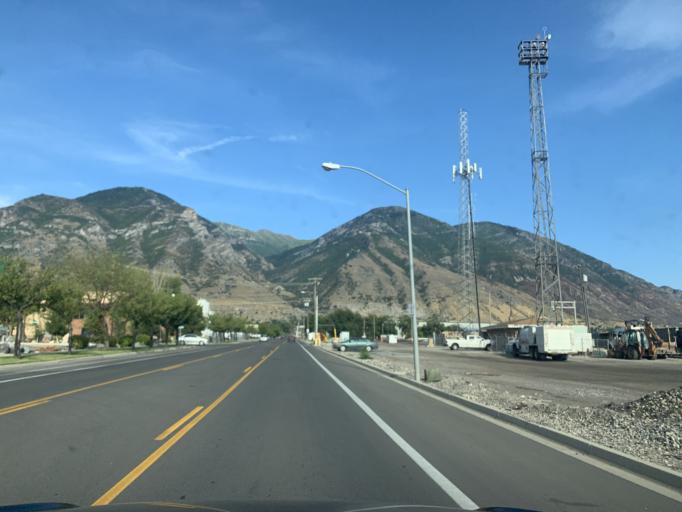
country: US
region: Utah
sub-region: Utah County
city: Provo
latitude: 40.2257
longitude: -111.6559
